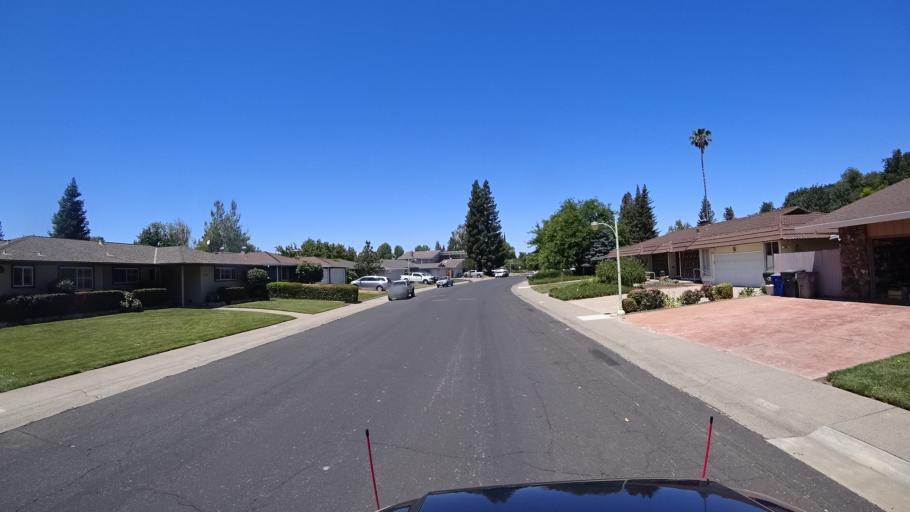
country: US
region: California
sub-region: Sacramento County
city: Parkway
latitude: 38.5093
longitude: -121.5181
